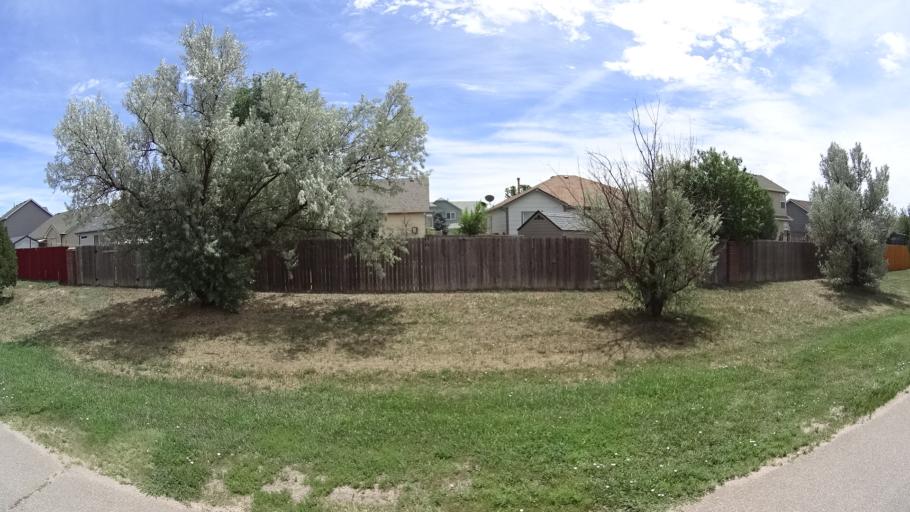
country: US
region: Colorado
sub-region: El Paso County
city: Fountain
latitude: 38.6678
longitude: -104.6797
